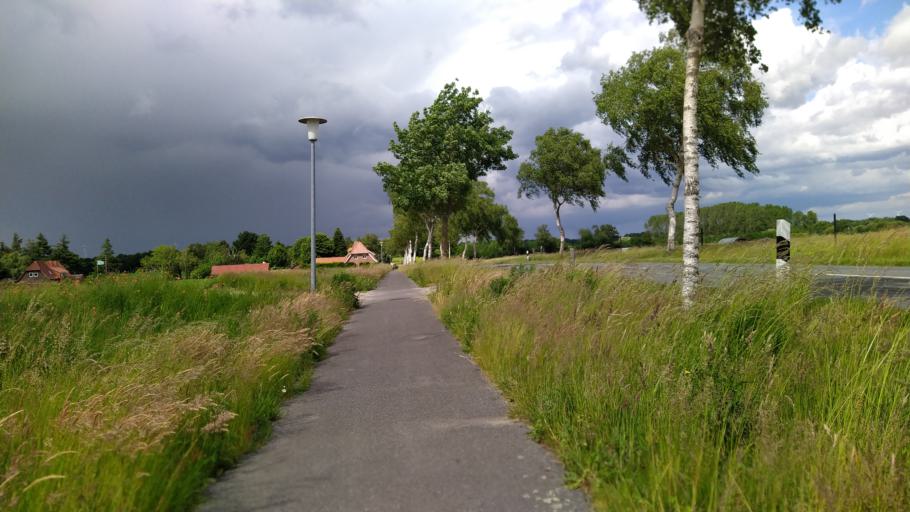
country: DE
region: Lower Saxony
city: Brest
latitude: 53.4539
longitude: 9.3833
